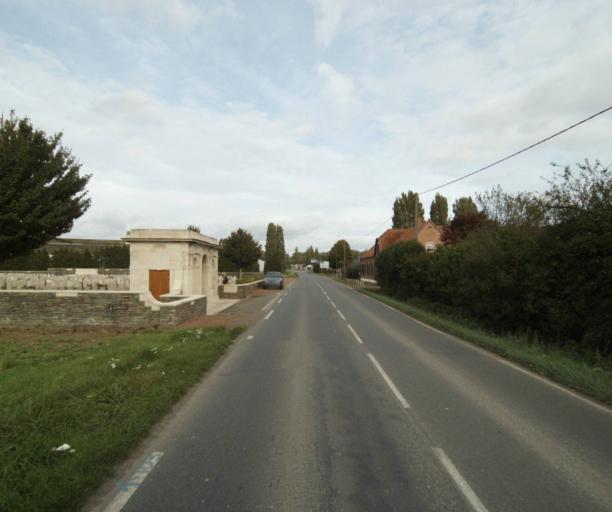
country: FR
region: Nord-Pas-de-Calais
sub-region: Departement du Nord
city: Bois-Grenier
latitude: 50.6573
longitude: 2.8880
